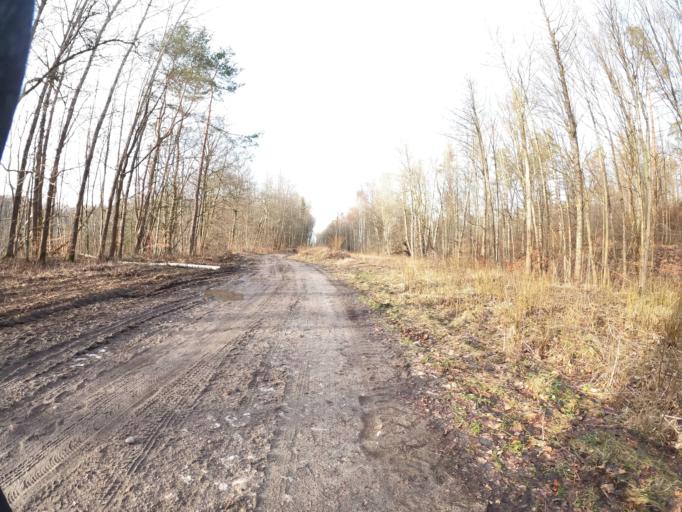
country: PL
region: West Pomeranian Voivodeship
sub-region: Powiat koszalinski
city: Polanow
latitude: 54.1698
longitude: 16.7513
